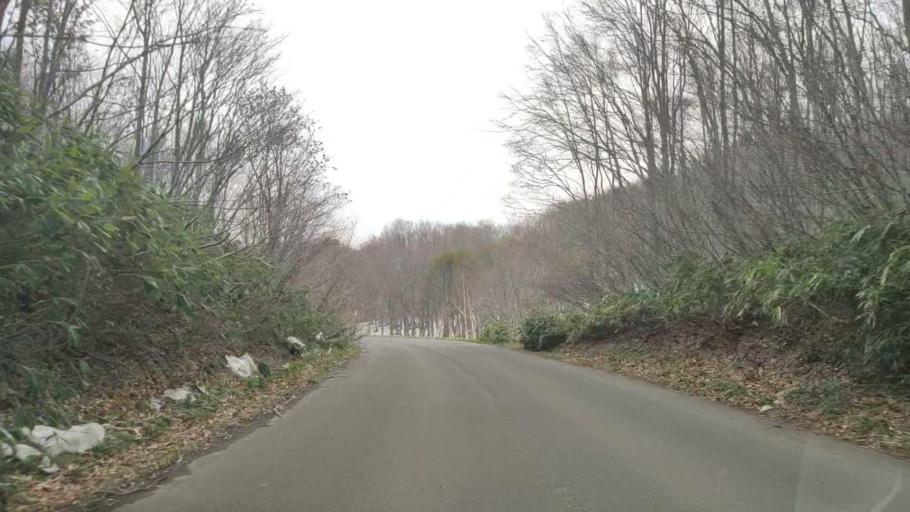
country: JP
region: Aomori
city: Aomori Shi
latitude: 40.6885
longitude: 140.9180
